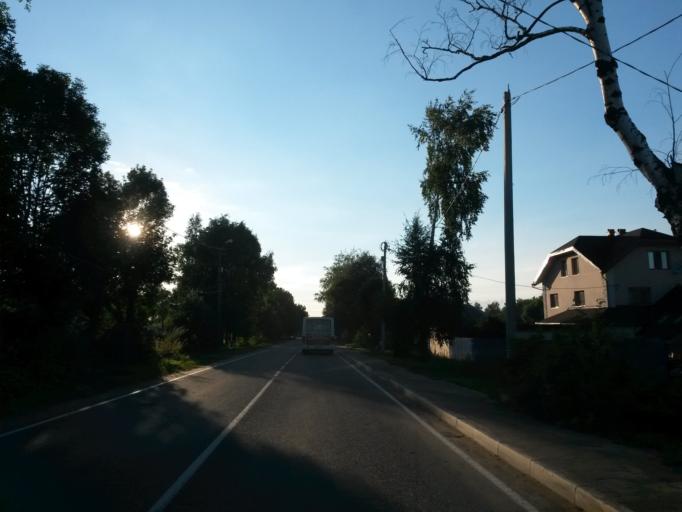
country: RU
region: Jaroslavl
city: Tutayev
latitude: 57.8719
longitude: 39.5280
